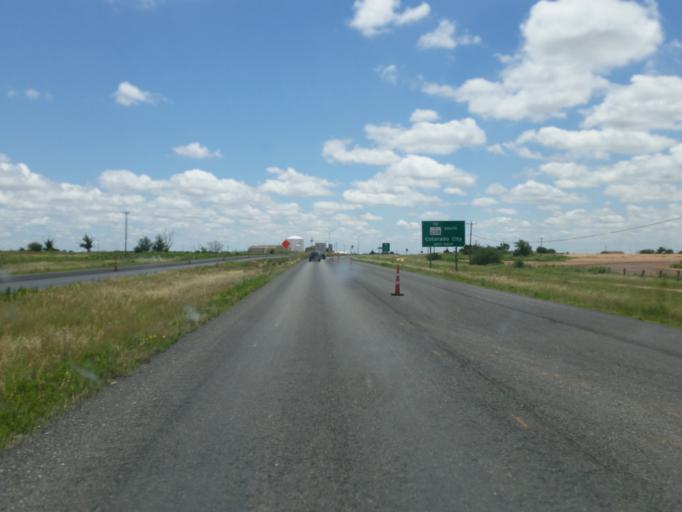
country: US
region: Texas
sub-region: Scurry County
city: Snyder
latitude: 32.7116
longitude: -100.8738
